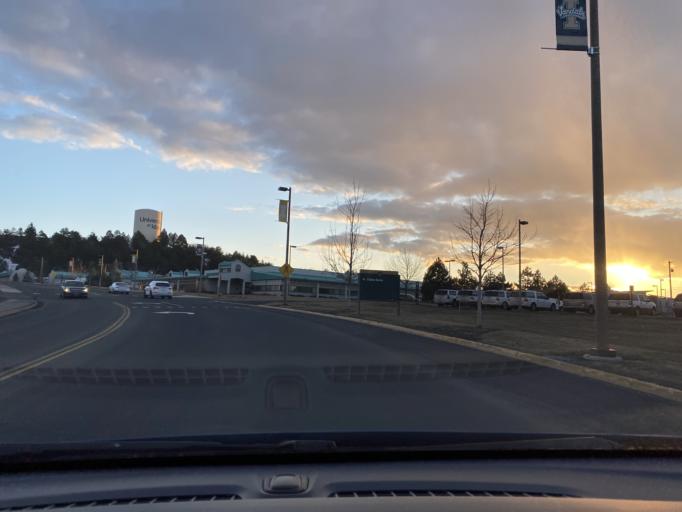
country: US
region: Idaho
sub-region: Latah County
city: Moscow
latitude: 46.7283
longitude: -117.0230
